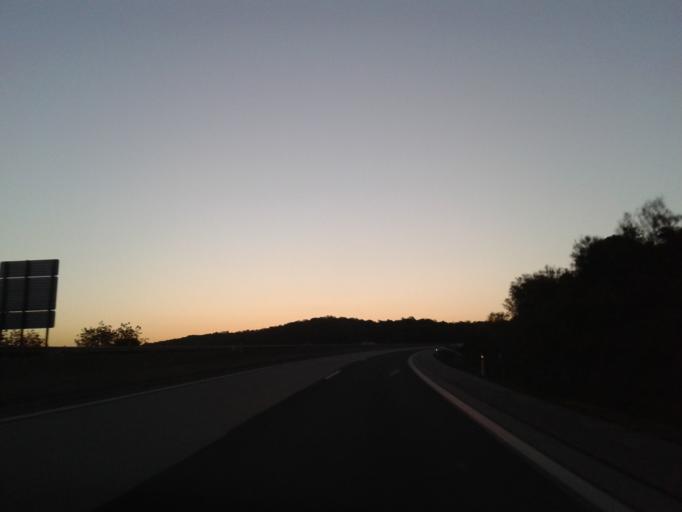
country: PT
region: Faro
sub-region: Loule
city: Boliqueime
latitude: 37.1594
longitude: -8.1838
